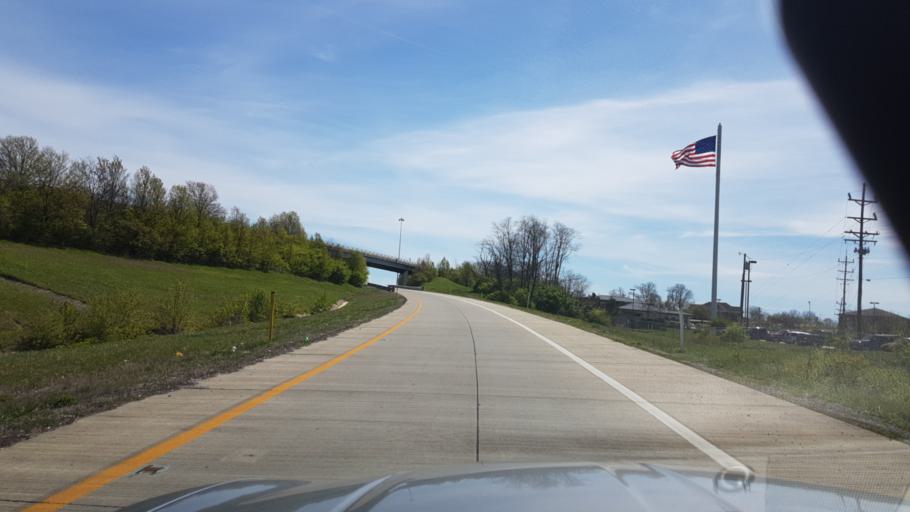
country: US
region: Kentucky
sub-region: Kenton County
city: Crestview Hills
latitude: 39.0269
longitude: -84.5768
